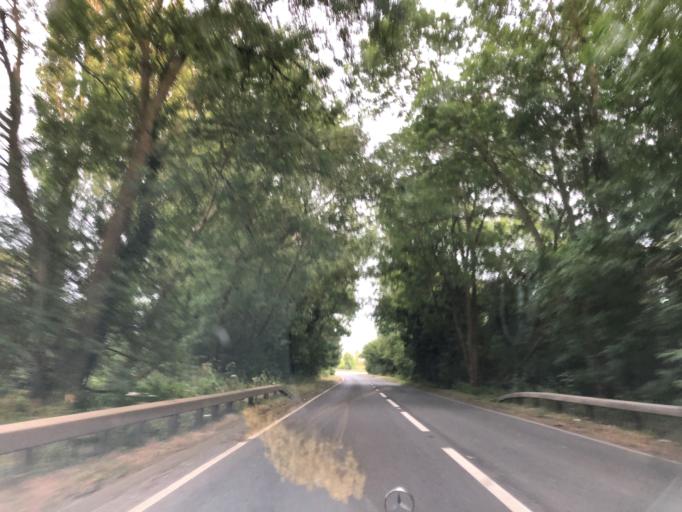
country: GB
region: England
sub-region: Solihull
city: Hampton in Arden
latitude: 52.4406
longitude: -1.6840
